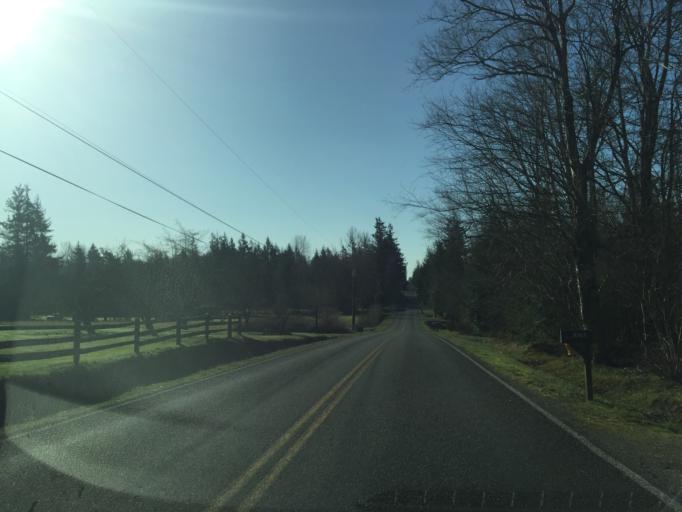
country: US
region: Washington
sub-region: Whatcom County
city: Marietta-Alderwood
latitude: 48.8132
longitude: -122.5080
